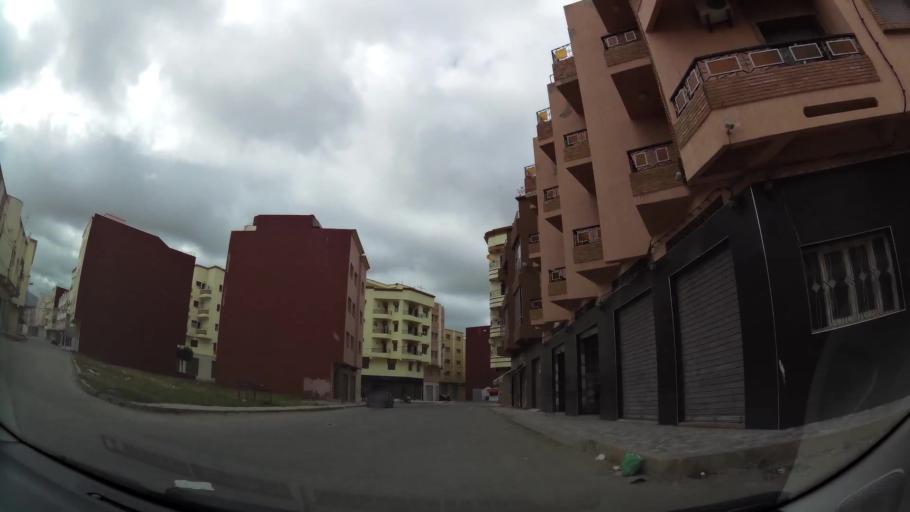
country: MA
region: Oriental
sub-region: Nador
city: Nador
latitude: 35.1668
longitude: -2.9353
